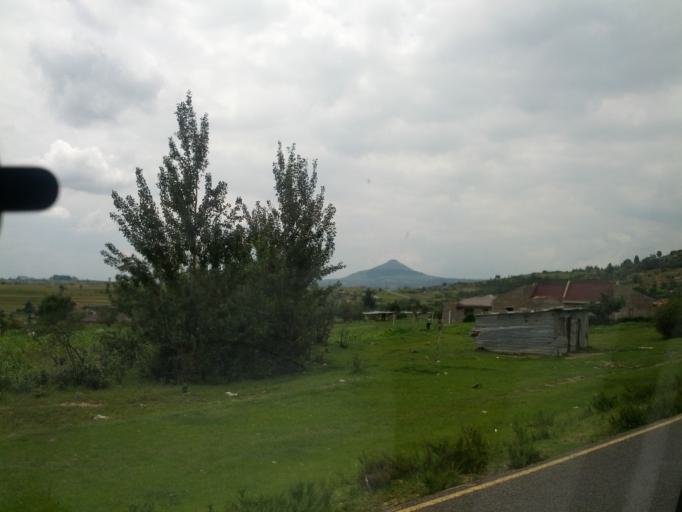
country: LS
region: Leribe
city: Leribe
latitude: -28.9598
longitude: 28.1724
